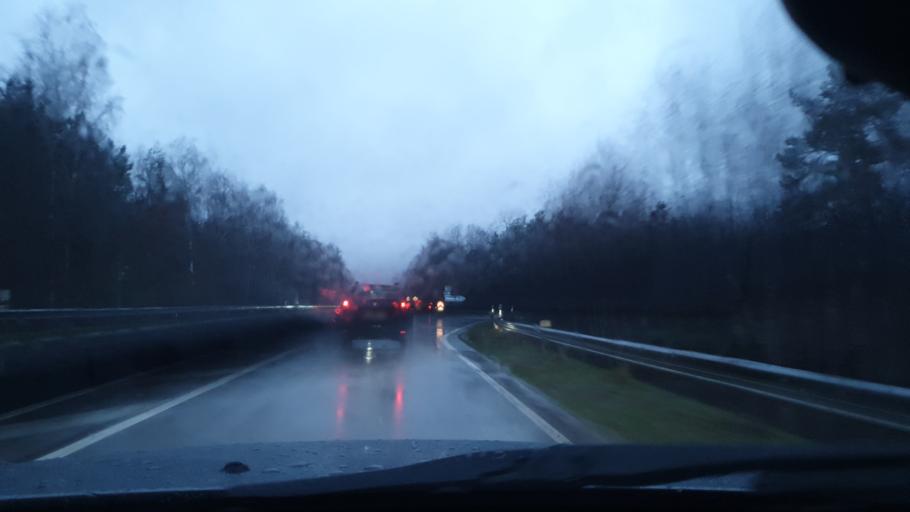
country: DE
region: Rheinland-Pfalz
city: Schonenberg-Kubelberg
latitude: 49.3695
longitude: 7.3700
